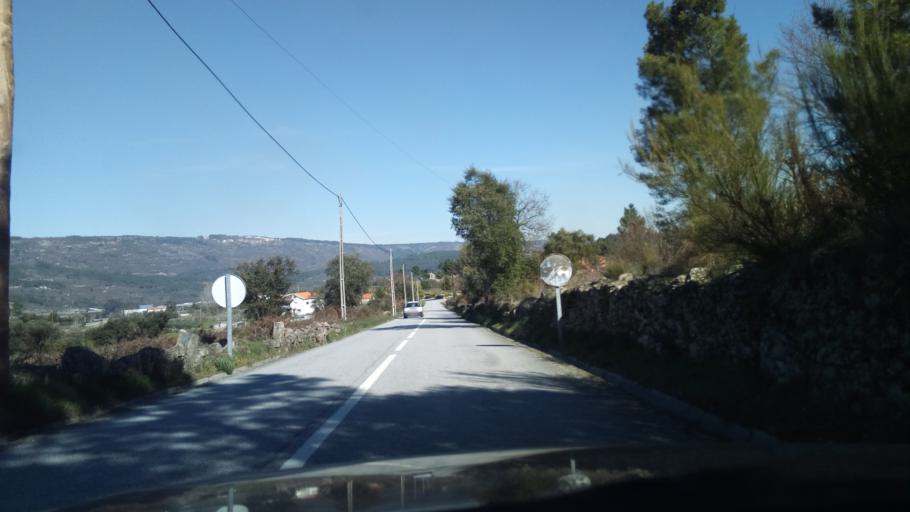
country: PT
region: Guarda
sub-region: Fornos de Algodres
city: Fornos de Algodres
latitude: 40.6030
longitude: -7.5145
